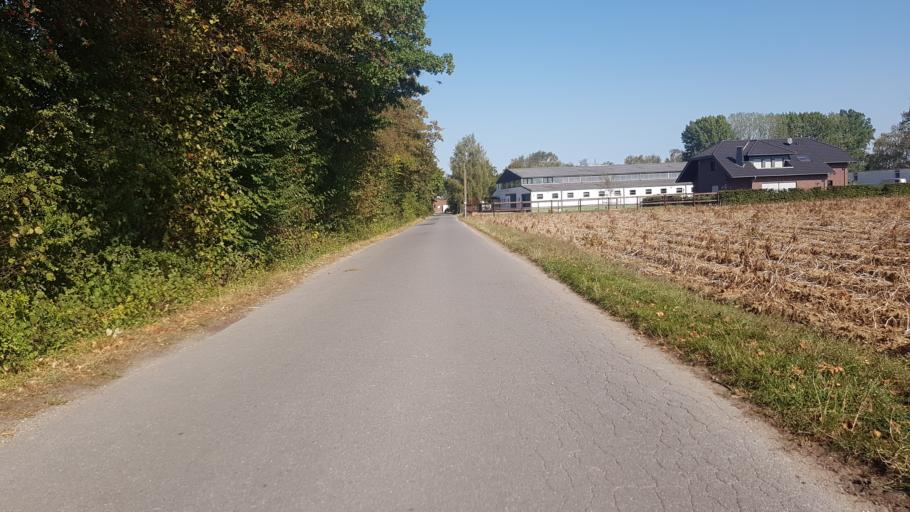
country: DE
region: North Rhine-Westphalia
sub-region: Regierungsbezirk Koln
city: Eschweiler
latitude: 50.8304
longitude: 6.2551
